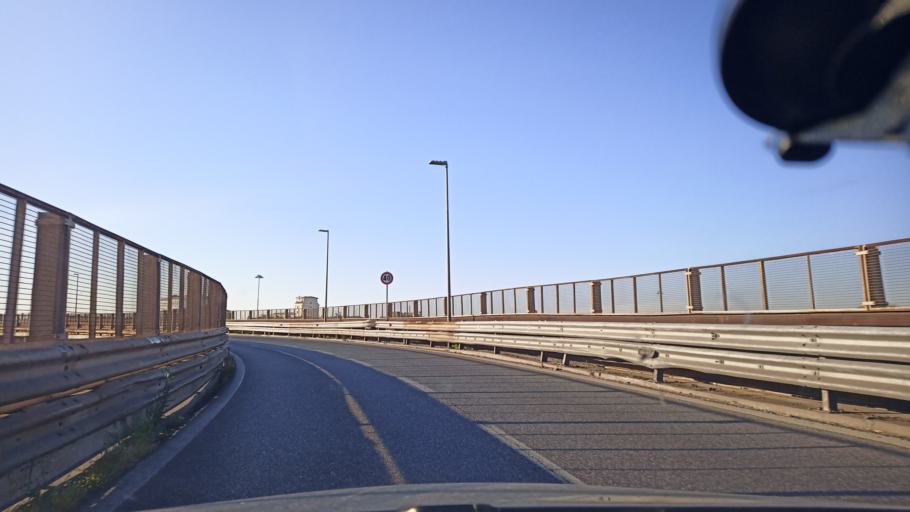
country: IT
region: Latium
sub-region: Citta metropolitana di Roma Capitale
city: Rome
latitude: 41.8944
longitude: 12.5174
